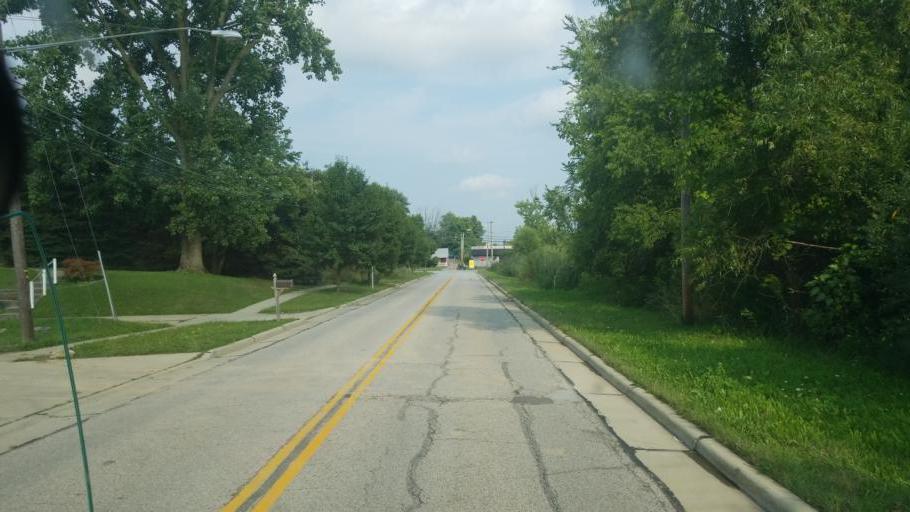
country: US
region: Ohio
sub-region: Medina County
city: Medina
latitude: 41.1425
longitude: -81.8887
